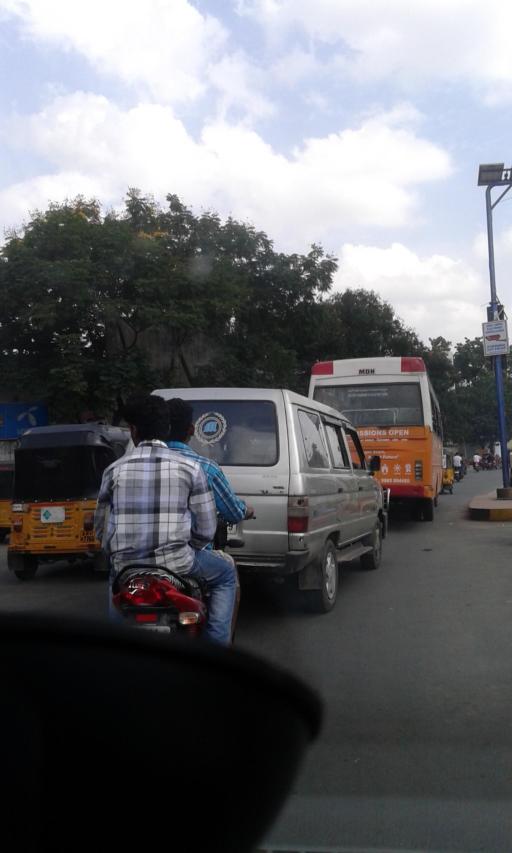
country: IN
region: Telangana
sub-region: Rangareddi
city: Gaddi Annaram
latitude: 17.3630
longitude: 78.5037
